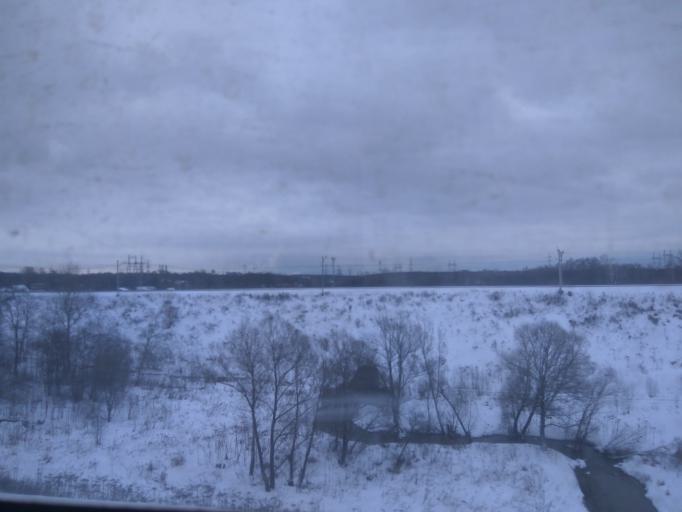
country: RU
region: Moscow
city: Annino
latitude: 55.5675
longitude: 37.6080
